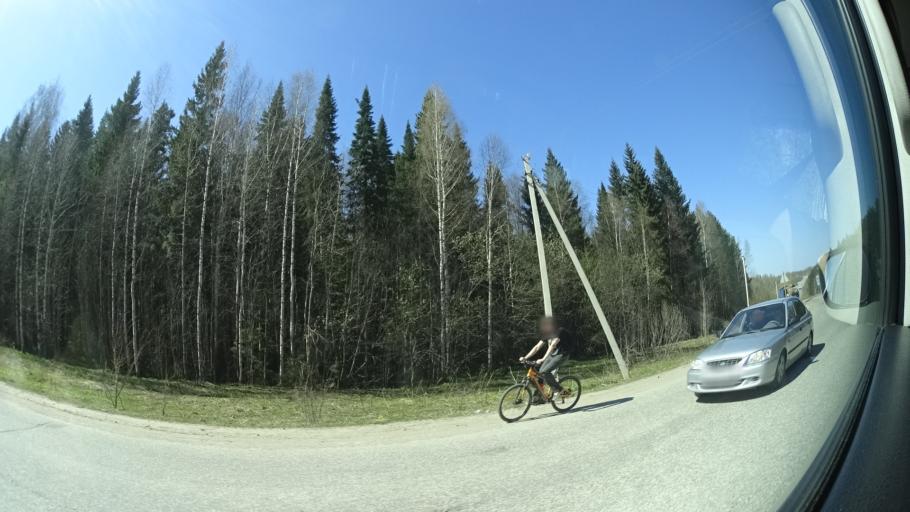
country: RU
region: Perm
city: Perm
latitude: 58.1356
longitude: 56.3039
